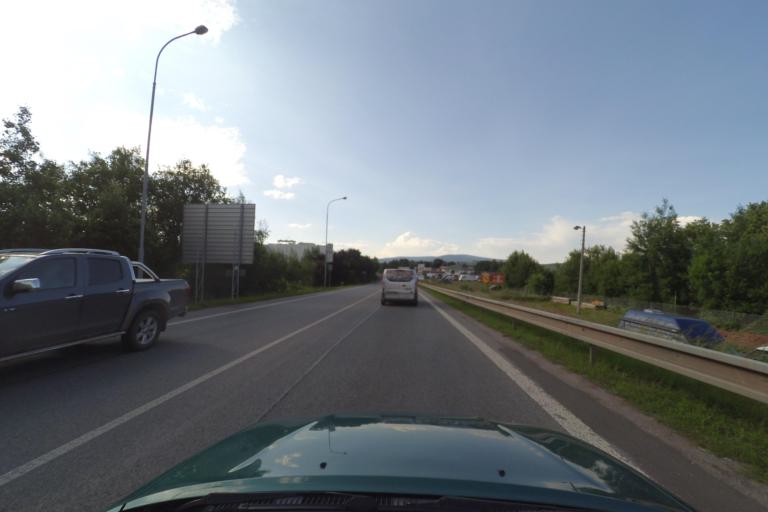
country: CZ
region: Kralovehradecky
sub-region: Okres Trutnov
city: Trutnov
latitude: 50.5694
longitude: 15.8954
